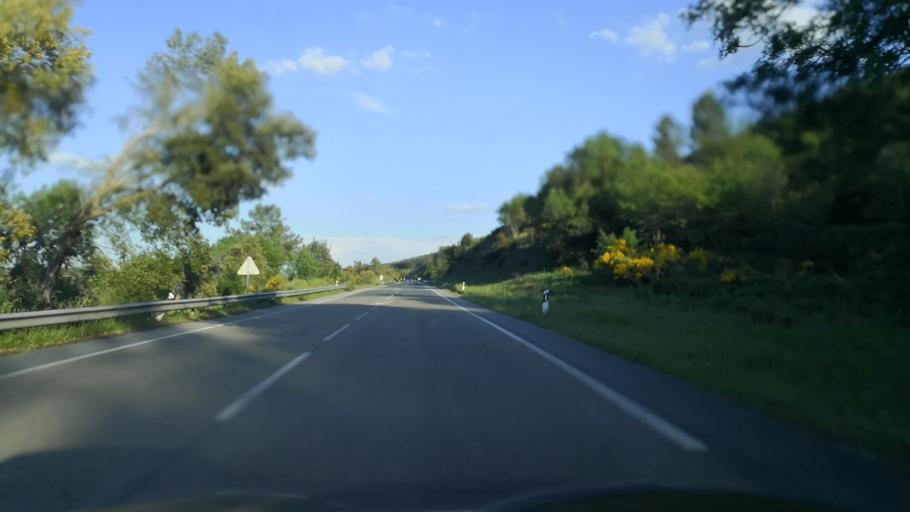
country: PT
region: Portalegre
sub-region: Marvao
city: Marvao
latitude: 39.3784
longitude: -7.3680
